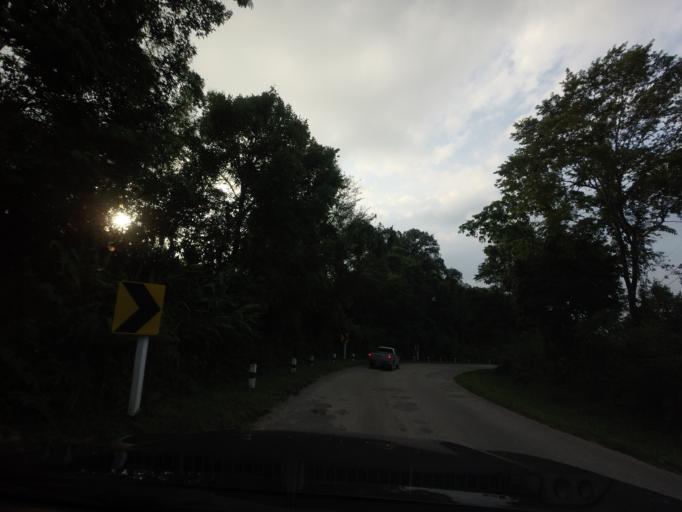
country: TH
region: Loei
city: Dan Sai
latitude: 17.3581
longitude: 101.0546
